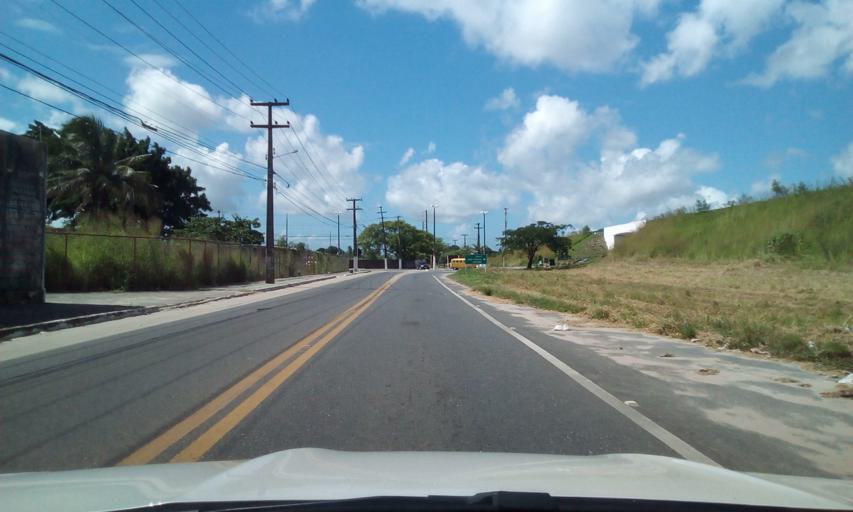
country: BR
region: Paraiba
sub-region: Santa Rita
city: Santa Rita
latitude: -7.1342
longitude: -34.9632
